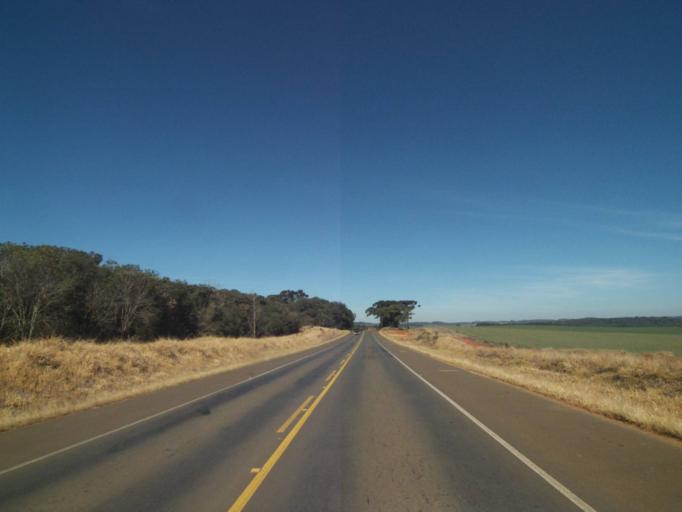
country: BR
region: Parana
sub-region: Tibagi
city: Tibagi
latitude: -24.7013
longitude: -50.4474
